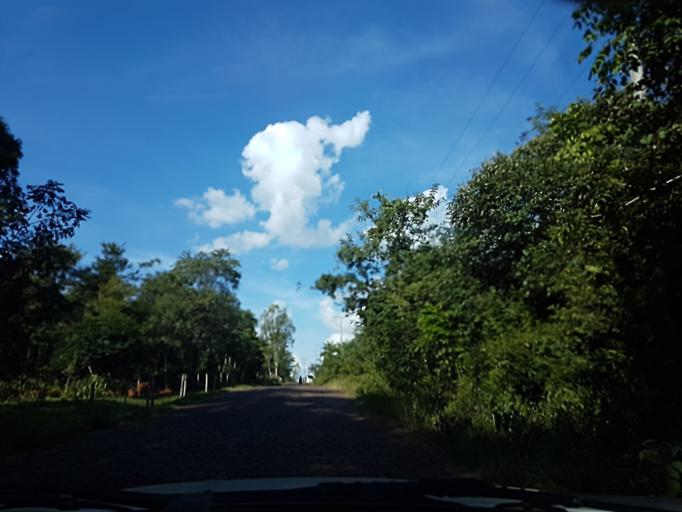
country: PY
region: Cordillera
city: Arroyos y Esteros
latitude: -24.9978
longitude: -57.1739
